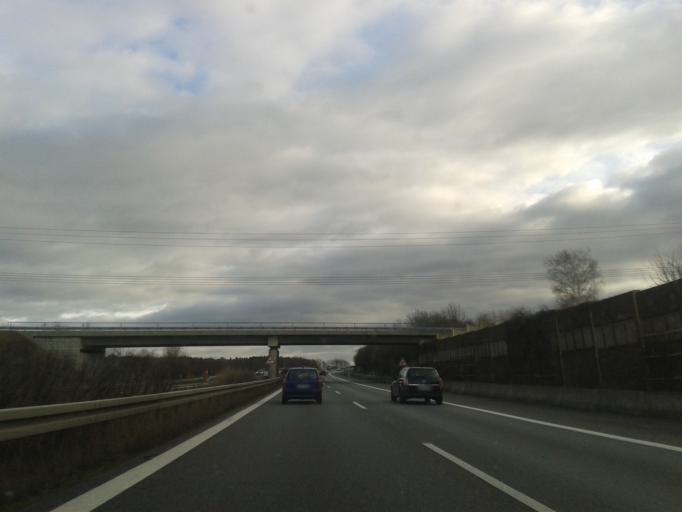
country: DE
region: Saxony
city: Wachau
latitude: 51.1705
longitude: 13.9069
